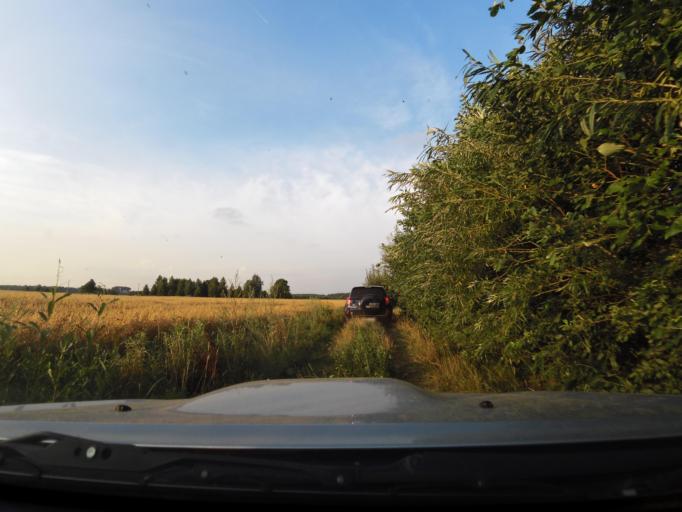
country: LT
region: Klaipedos apskritis
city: Silute
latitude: 55.4720
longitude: 21.4674
